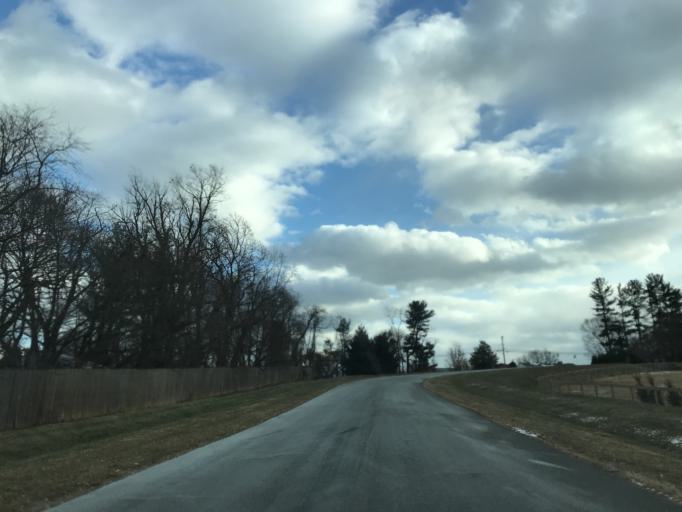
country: US
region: Maryland
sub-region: Harford County
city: Bel Air North
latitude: 39.6107
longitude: -76.3853
